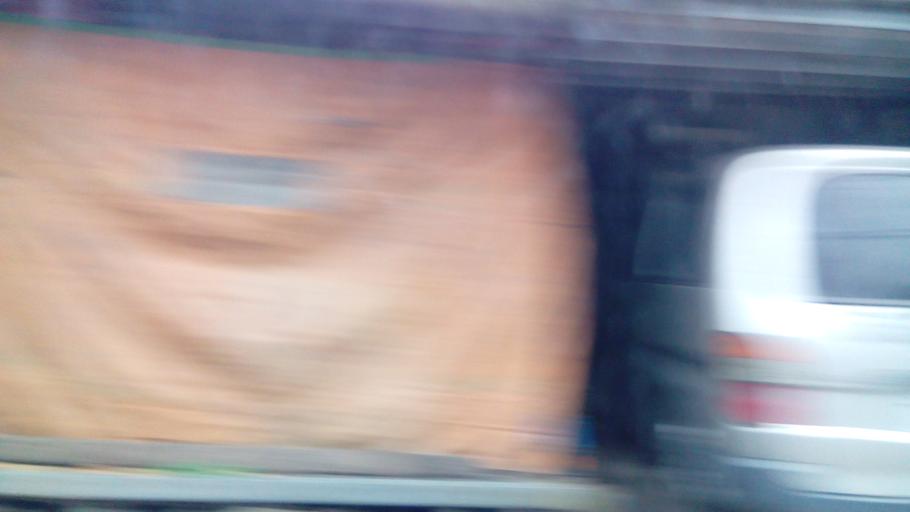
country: TW
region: Taiwan
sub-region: Nantou
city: Puli
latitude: 24.2595
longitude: 121.2569
